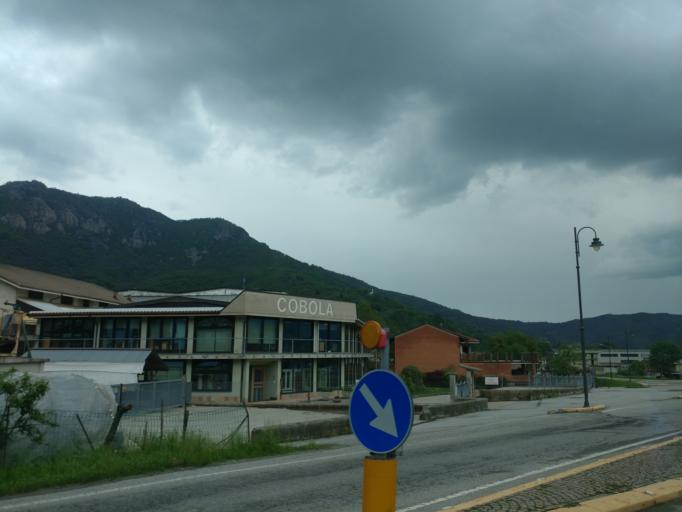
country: IT
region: Piedmont
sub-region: Provincia di Cuneo
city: Sanfront
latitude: 44.6477
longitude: 7.3239
